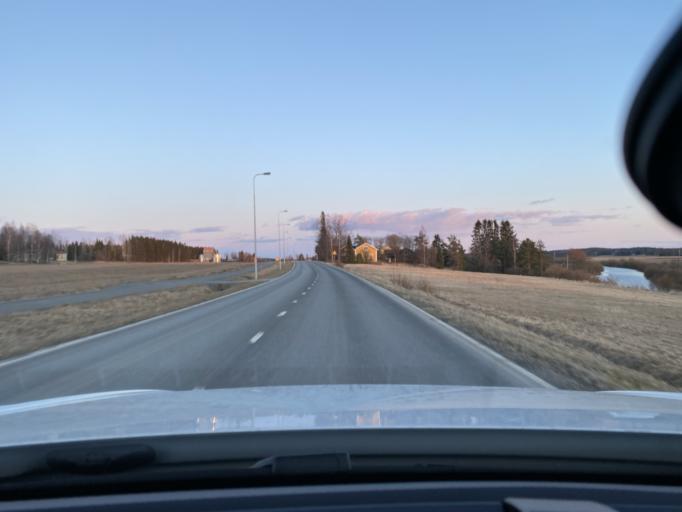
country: FI
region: Pirkanmaa
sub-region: Lounais-Pirkanmaa
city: Punkalaidun
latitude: 61.1079
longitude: 23.1304
